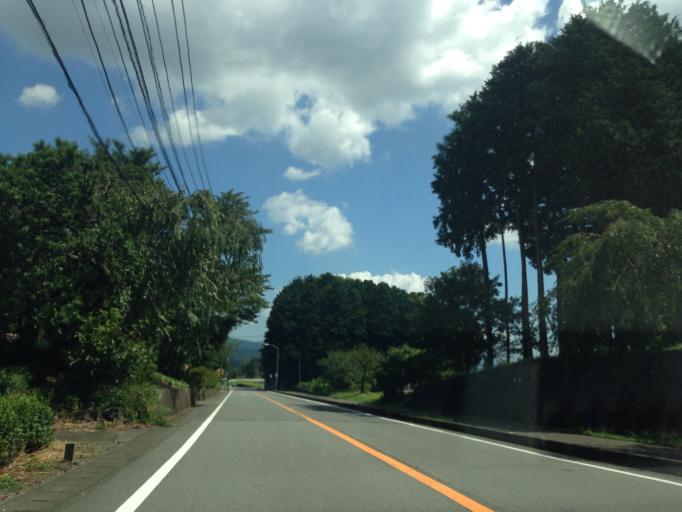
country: JP
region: Shizuoka
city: Gotemba
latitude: 35.2181
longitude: 138.8929
